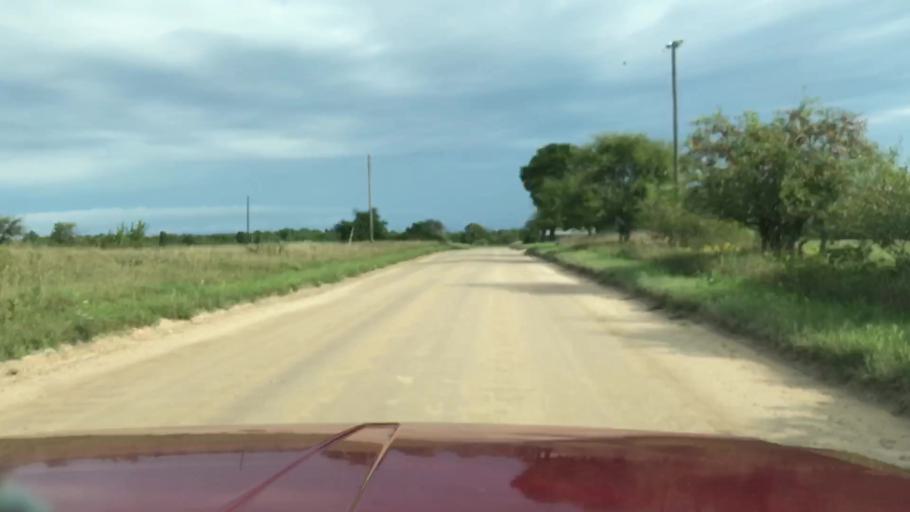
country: US
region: Michigan
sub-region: Charlevoix County
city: Charlevoix
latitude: 45.7250
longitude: -85.5158
